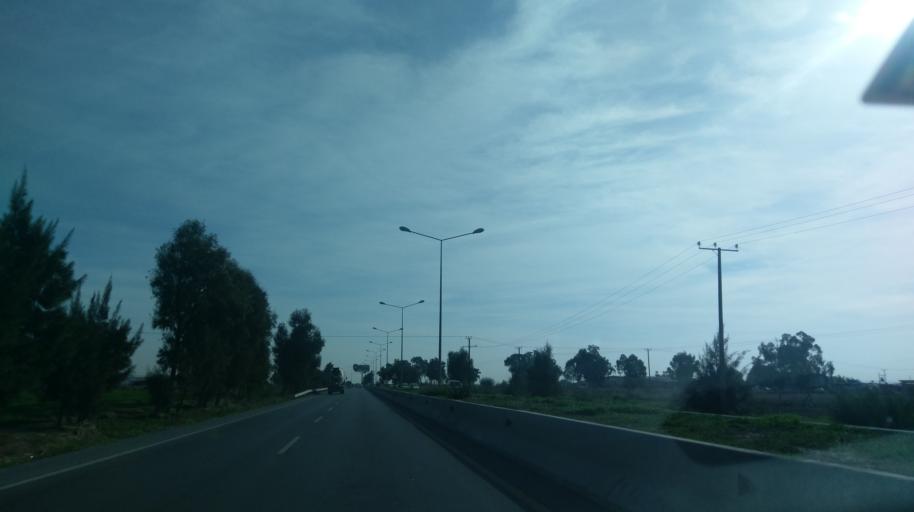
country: CY
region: Lefkosia
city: Nicosia
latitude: 35.2141
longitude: 33.4414
